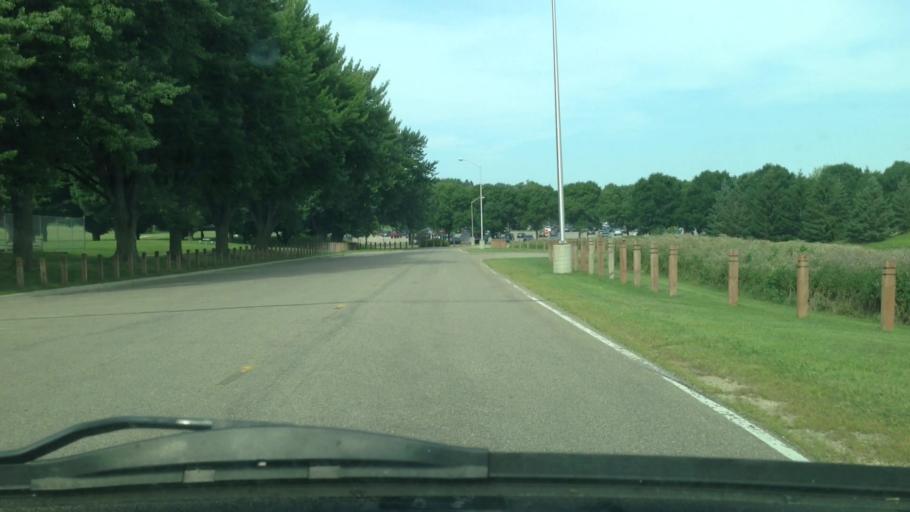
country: US
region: Minnesota
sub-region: Olmsted County
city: Rochester
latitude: 44.0565
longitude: -92.4994
